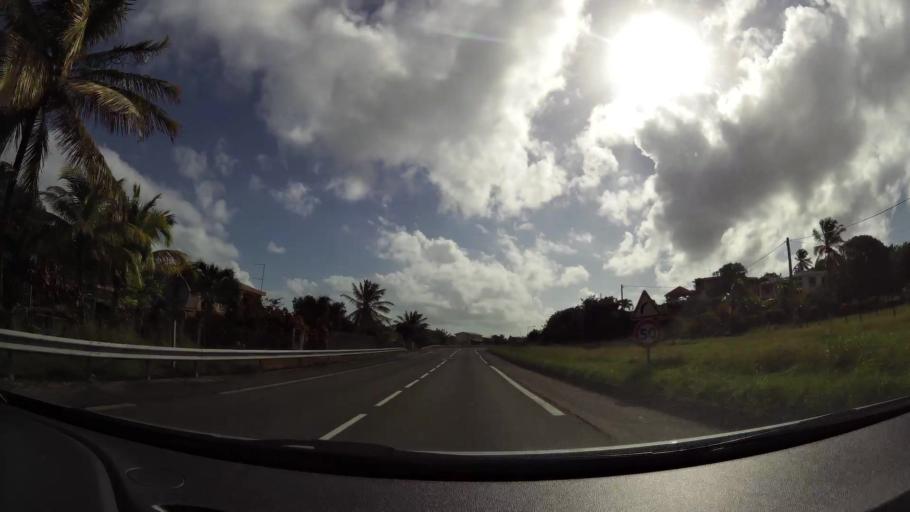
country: MQ
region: Martinique
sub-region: Martinique
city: Le Francois
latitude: 14.5935
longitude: -60.8713
